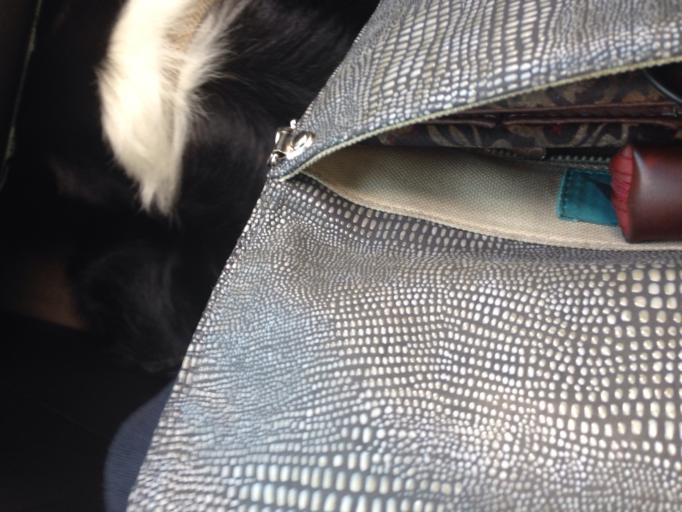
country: MX
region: Baja California
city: Tijuana
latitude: 32.4971
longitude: -117.0016
